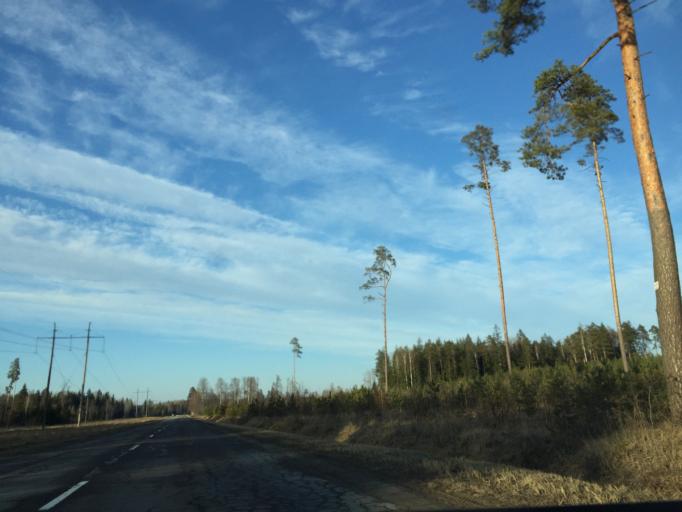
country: LV
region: Kekava
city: Balozi
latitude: 56.7930
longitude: 24.0756
